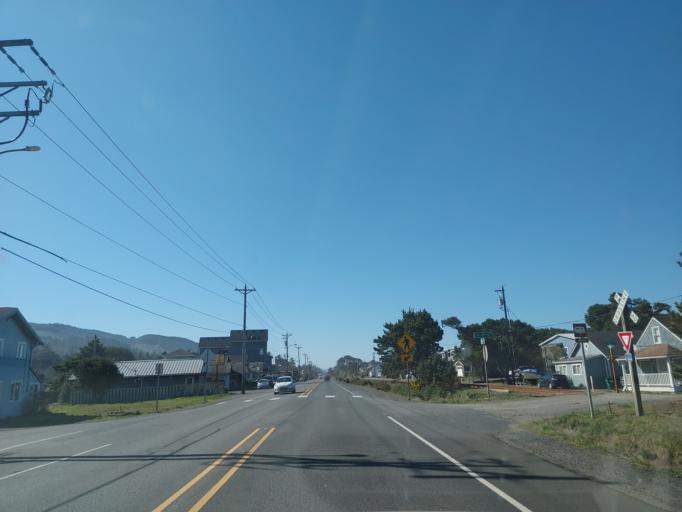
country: US
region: Oregon
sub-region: Tillamook County
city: Rockaway Beach
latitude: 45.6081
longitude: -123.9447
